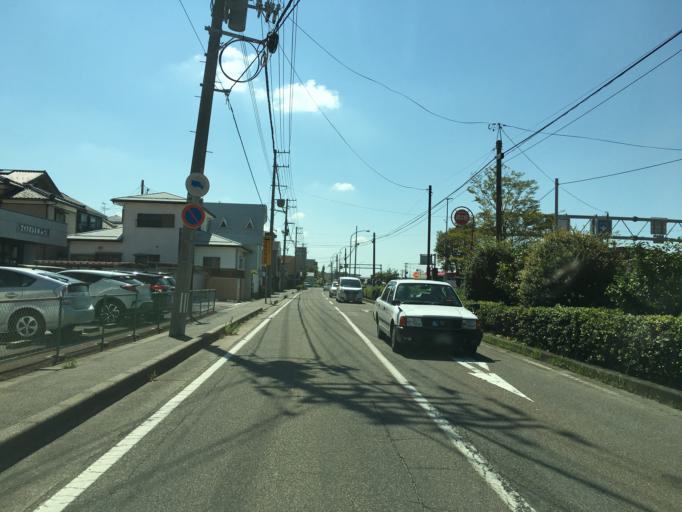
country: JP
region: Niigata
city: Niigata-shi
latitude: 37.9010
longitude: 139.0144
